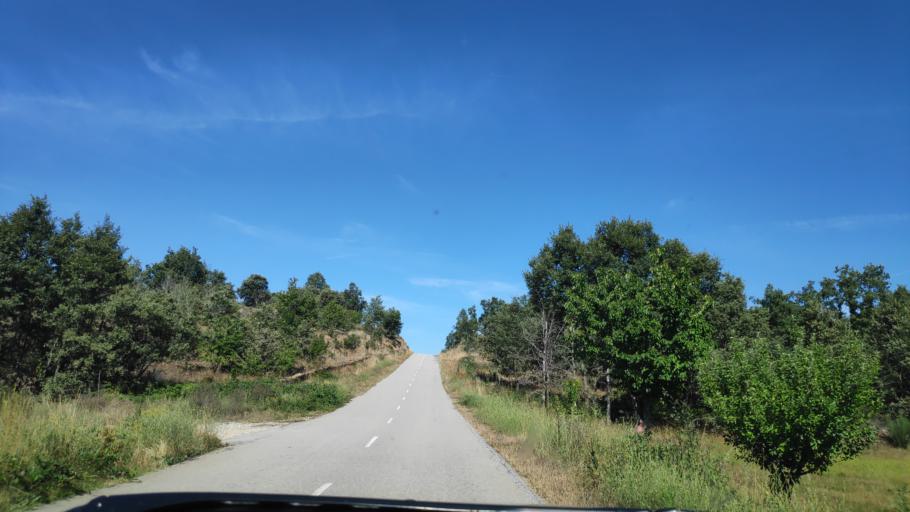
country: ES
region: Castille and Leon
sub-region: Provincia de Zamora
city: Alcanices
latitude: 41.6425
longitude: -6.3557
